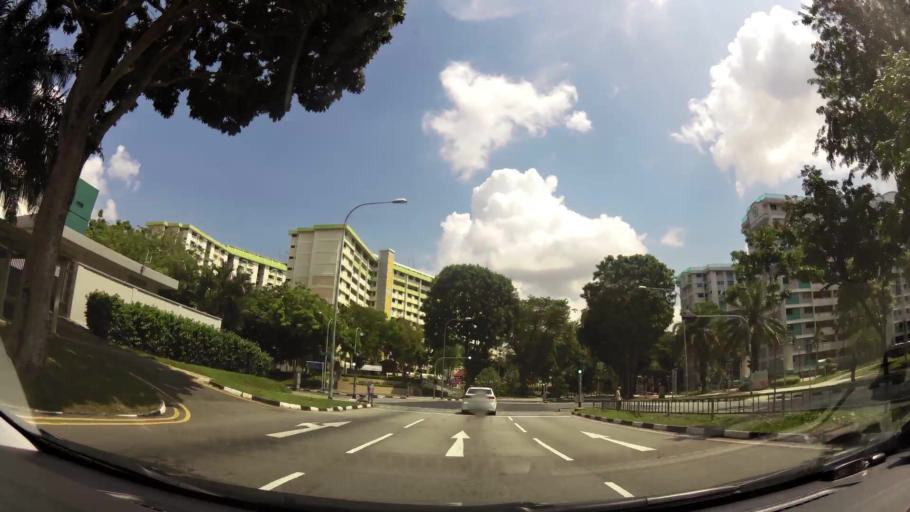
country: SG
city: Singapore
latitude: 1.3692
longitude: 103.8369
